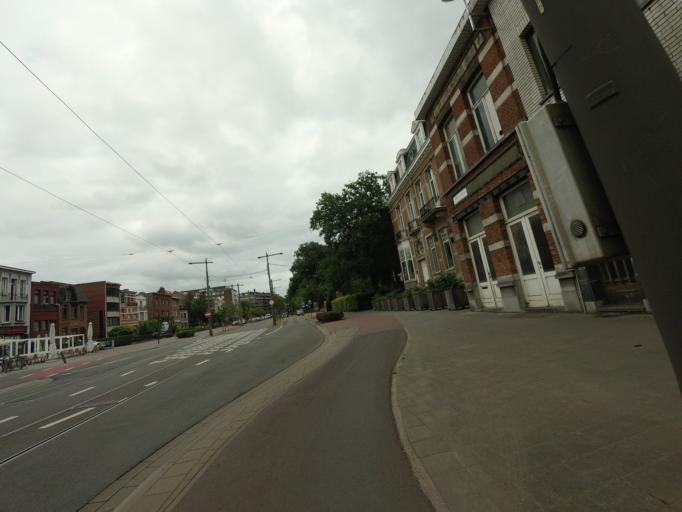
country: BE
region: Flanders
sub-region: Provincie Antwerpen
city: Borsbeek
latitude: 51.2200
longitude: 4.4658
